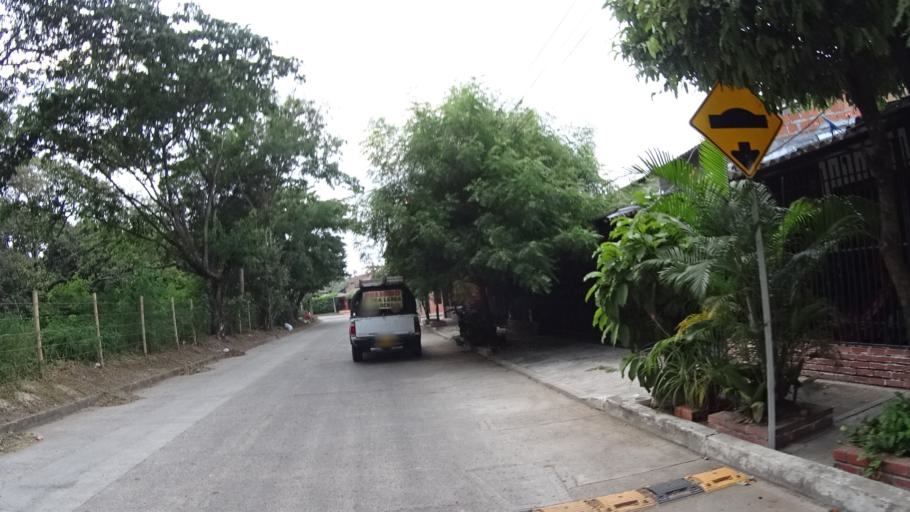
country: CO
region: Cundinamarca
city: Puerto Salgar
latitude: 5.4795
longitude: -74.6728
